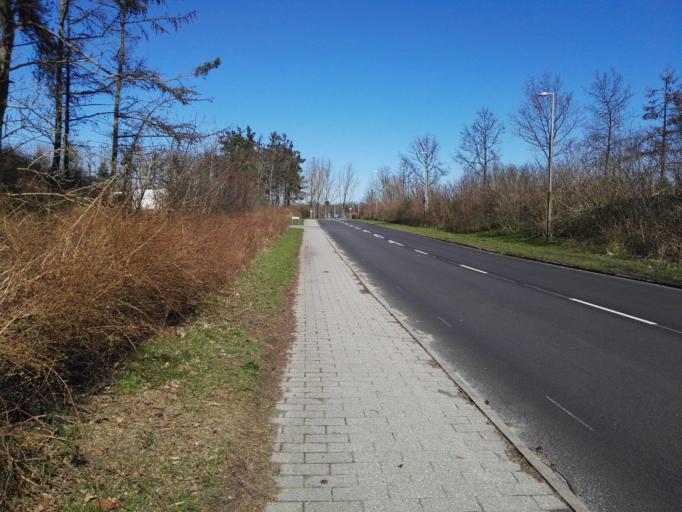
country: DK
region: Capital Region
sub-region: Egedal Kommune
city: Olstykke
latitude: 55.7859
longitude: 12.1753
